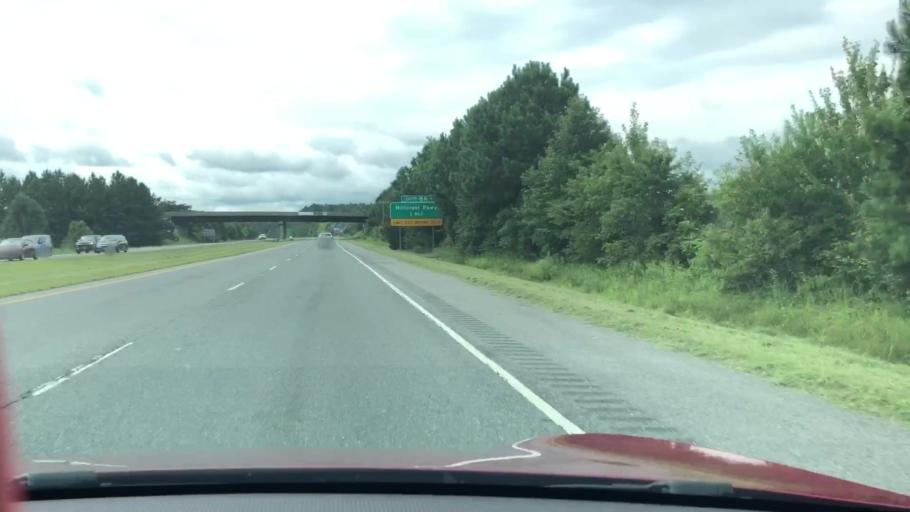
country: US
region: Virginia
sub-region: City of Chesapeake
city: Chesapeake
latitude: 36.6767
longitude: -76.2298
